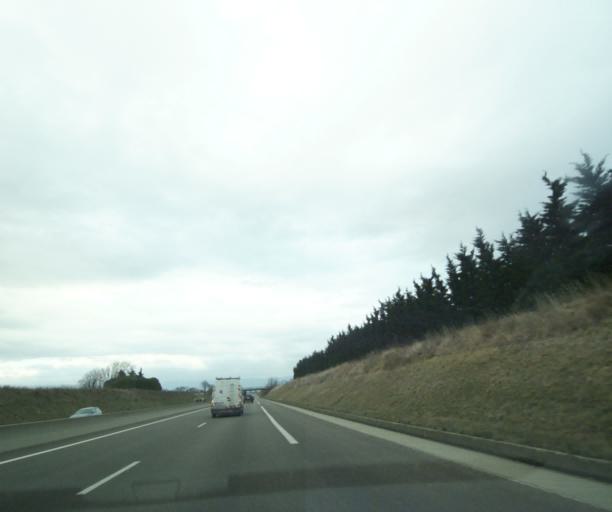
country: FR
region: Rhone-Alpes
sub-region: Departement de la Drome
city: Bourg-les-Valence
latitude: 44.9622
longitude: 4.9218
